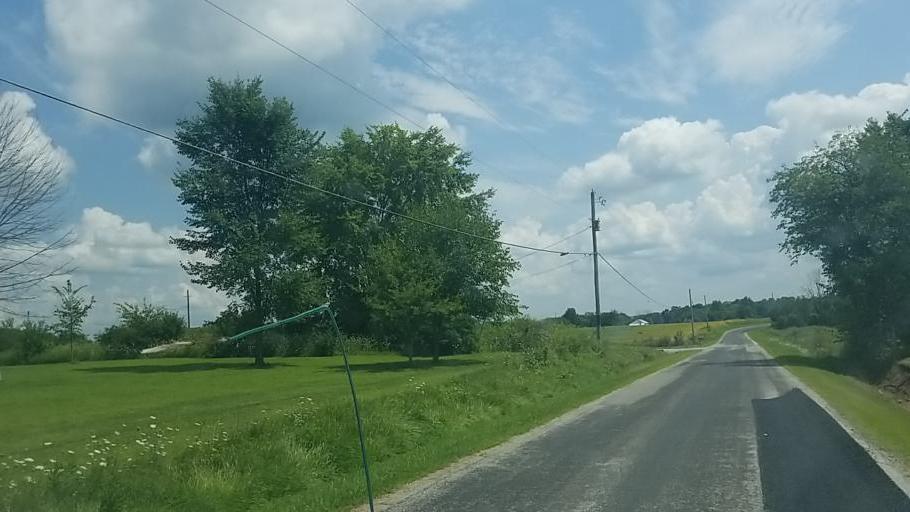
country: US
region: Ohio
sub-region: Wayne County
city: West Salem
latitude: 41.0296
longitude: -82.0855
